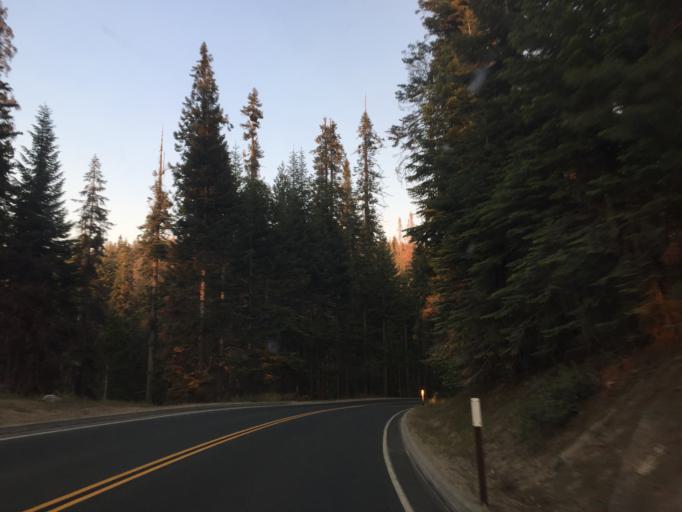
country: US
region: California
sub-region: Fresno County
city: Squaw Valley
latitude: 36.7521
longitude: -118.9623
